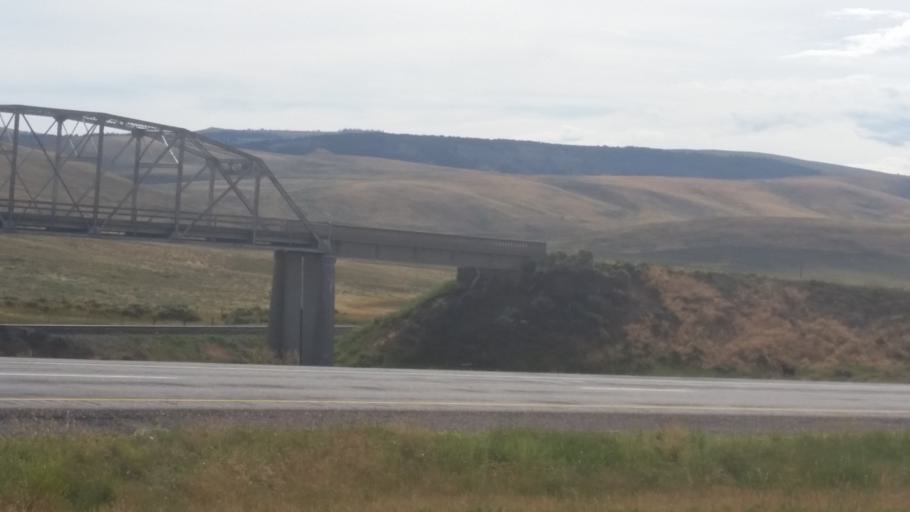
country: US
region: Idaho
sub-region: Clark County
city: Dubois
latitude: 44.5492
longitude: -112.2990
